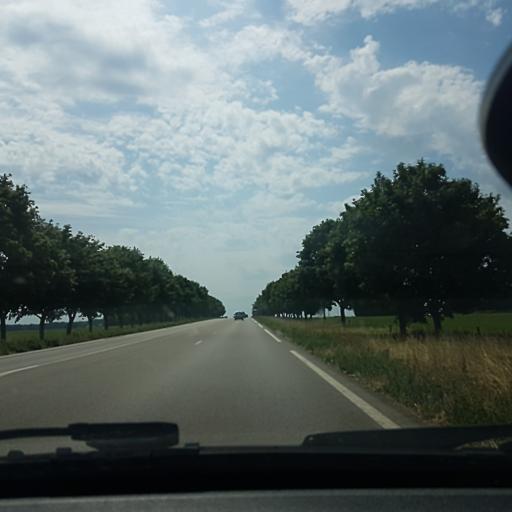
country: FR
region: Bourgogne
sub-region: Departement de Saone-et-Loire
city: Chagny
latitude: 46.8956
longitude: 4.7634
